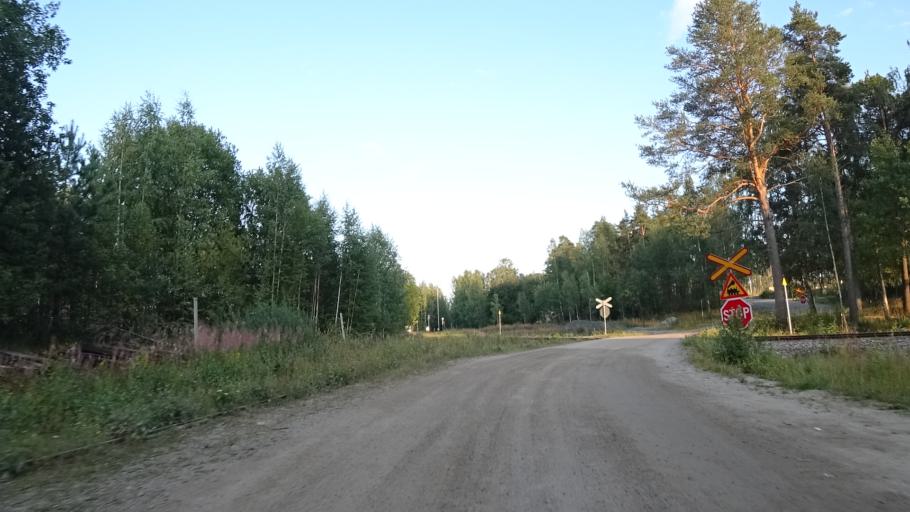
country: FI
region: Southern Savonia
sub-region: Savonlinna
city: Punkaharju
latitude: 61.7597
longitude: 29.3838
